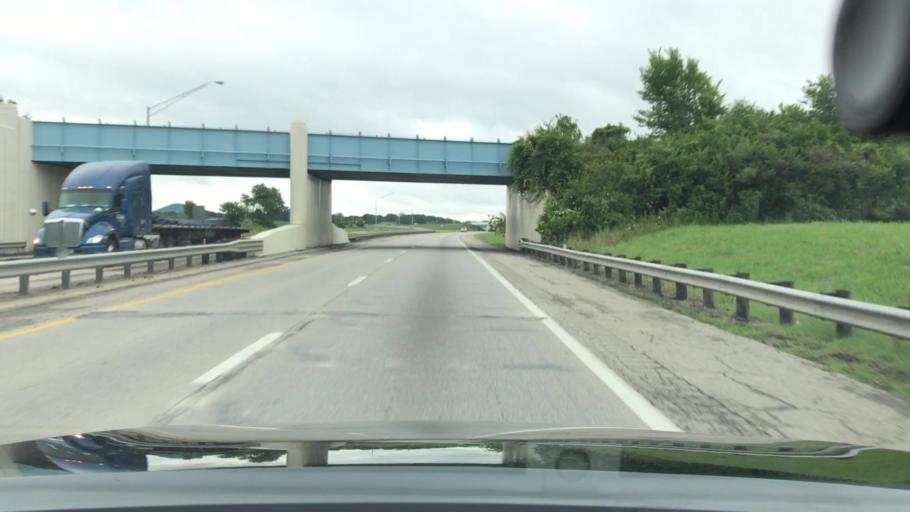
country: US
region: Ohio
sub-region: Ross County
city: Chillicothe
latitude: 39.3029
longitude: -82.9162
